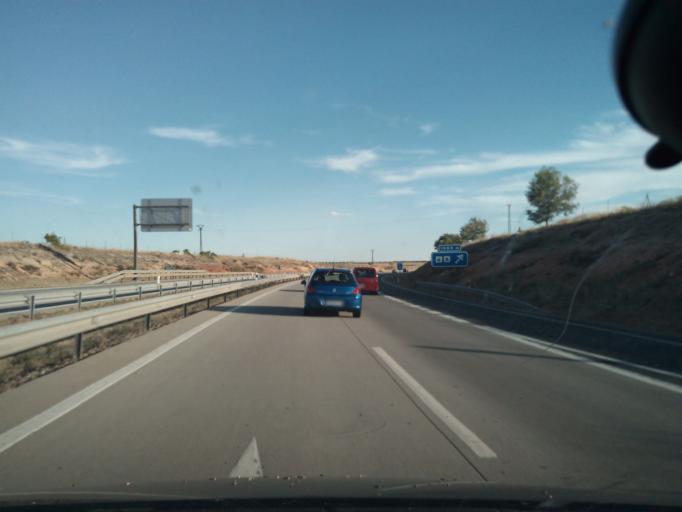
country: ES
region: Castille-La Mancha
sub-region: Province of Toledo
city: Dosbarrios
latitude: 39.8873
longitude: -3.4709
